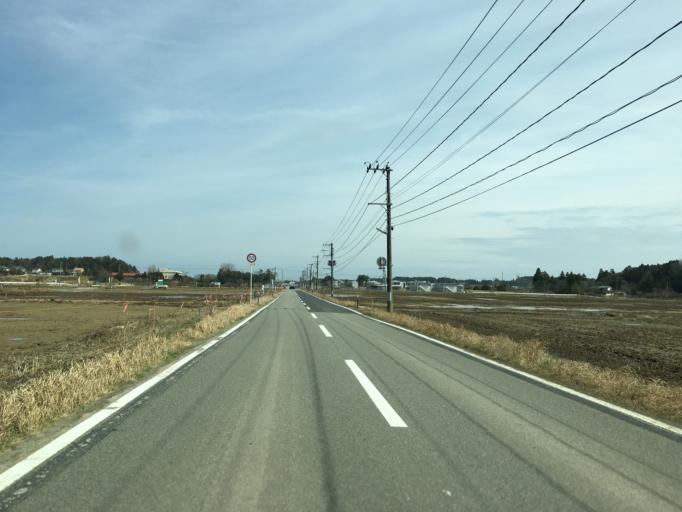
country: JP
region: Fukushima
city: Namie
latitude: 37.4564
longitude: 140.9964
